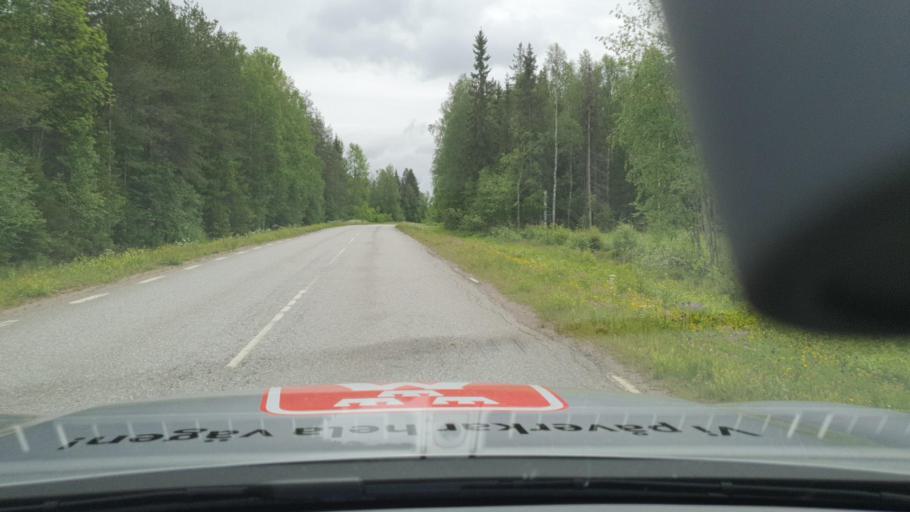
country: SE
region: Norrbotten
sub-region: Lulea Kommun
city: Ranea
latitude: 65.8798
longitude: 22.2105
